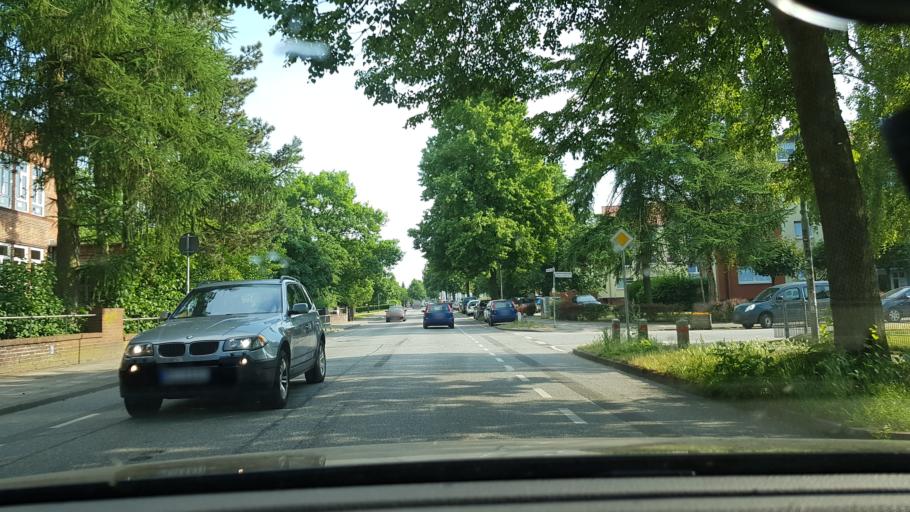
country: DE
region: Schleswig-Holstein
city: Luebeck
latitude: 53.8474
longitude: 10.6988
